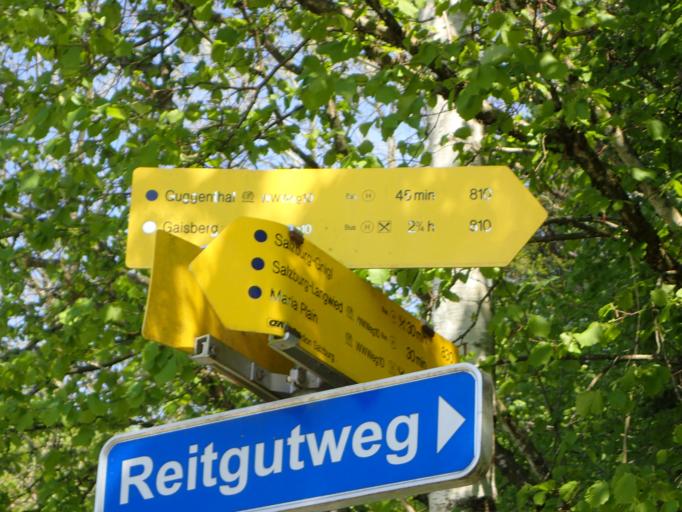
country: AT
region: Salzburg
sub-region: Politischer Bezirk Salzburg-Umgebung
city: Hallwang
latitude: 47.8216
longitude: 13.0859
